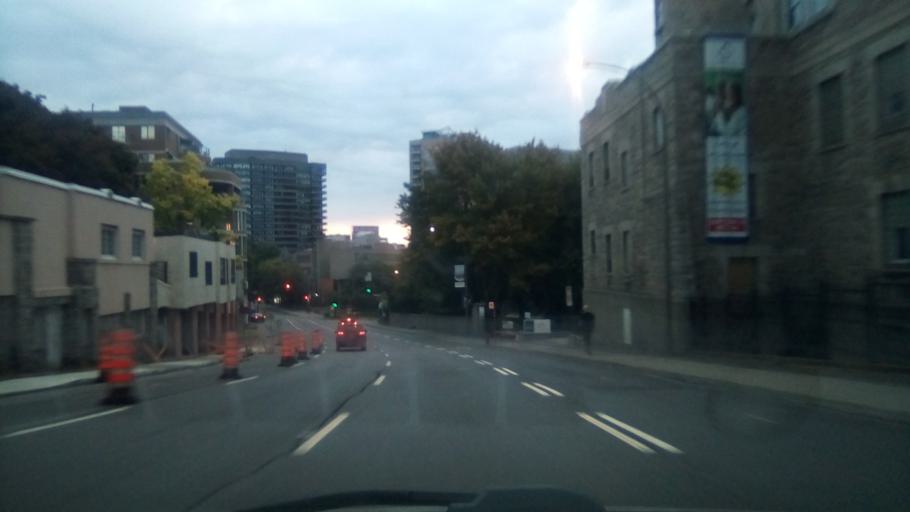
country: CA
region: Quebec
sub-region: Montreal
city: Montreal
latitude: 45.4954
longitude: -73.5882
